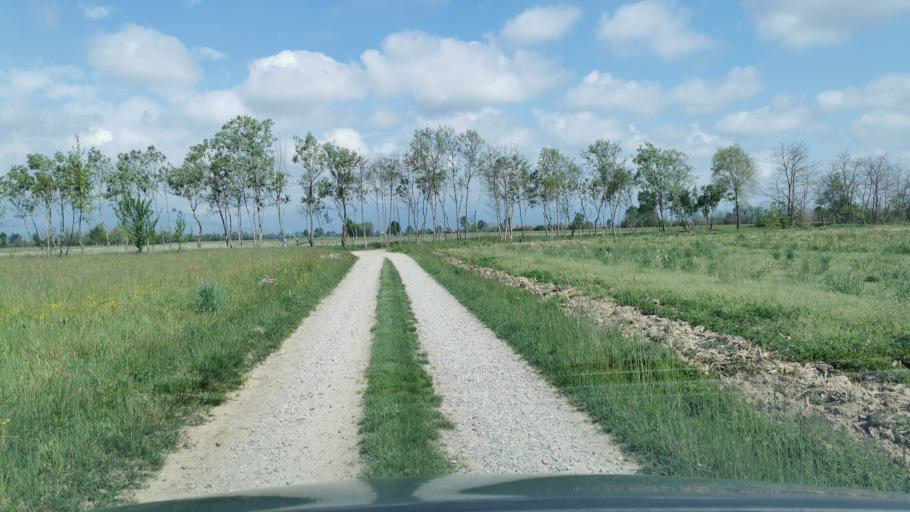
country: IT
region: Piedmont
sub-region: Provincia di Torino
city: Rivarossa
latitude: 45.2763
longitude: 7.7155
